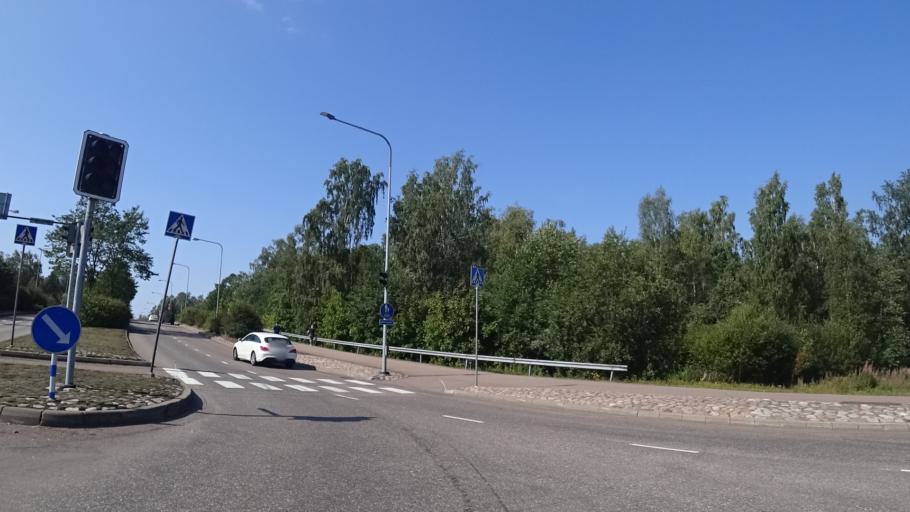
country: FI
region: Kymenlaakso
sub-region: Kotka-Hamina
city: Karhula
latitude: 60.5153
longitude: 26.9462
